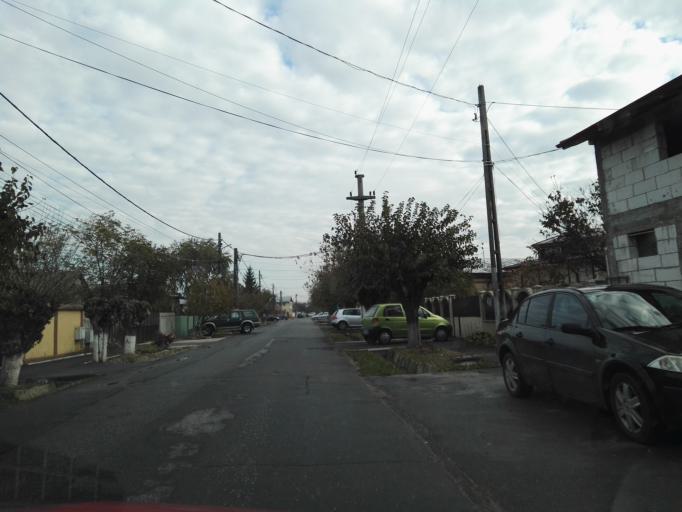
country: RO
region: Ilfov
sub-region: Comuna Jilava
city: Jilava
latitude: 44.3398
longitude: 26.0723
